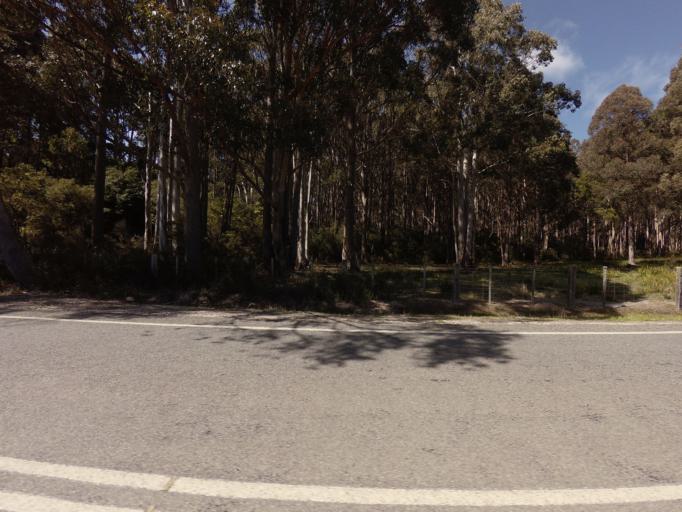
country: AU
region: Tasmania
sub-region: Derwent Valley
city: New Norfolk
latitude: -42.7227
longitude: 146.6791
